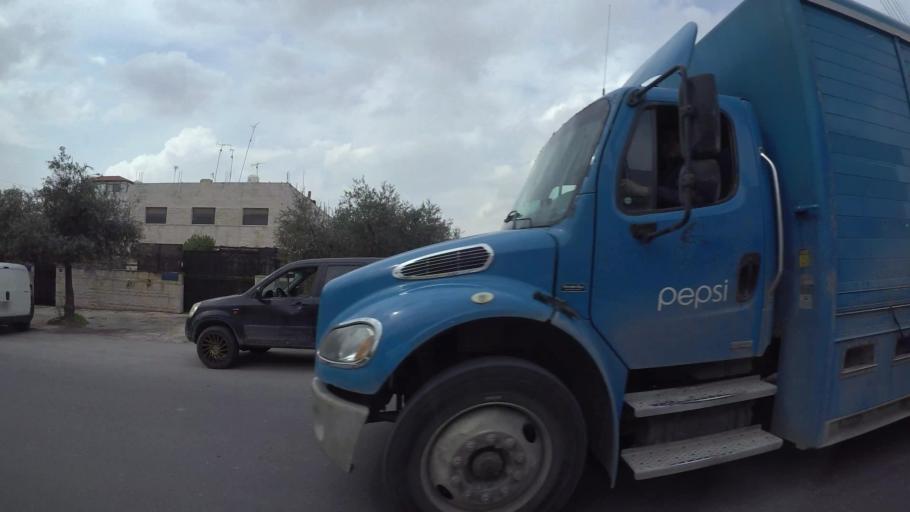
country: JO
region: Amman
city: Umm as Summaq
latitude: 31.8926
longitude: 35.8609
